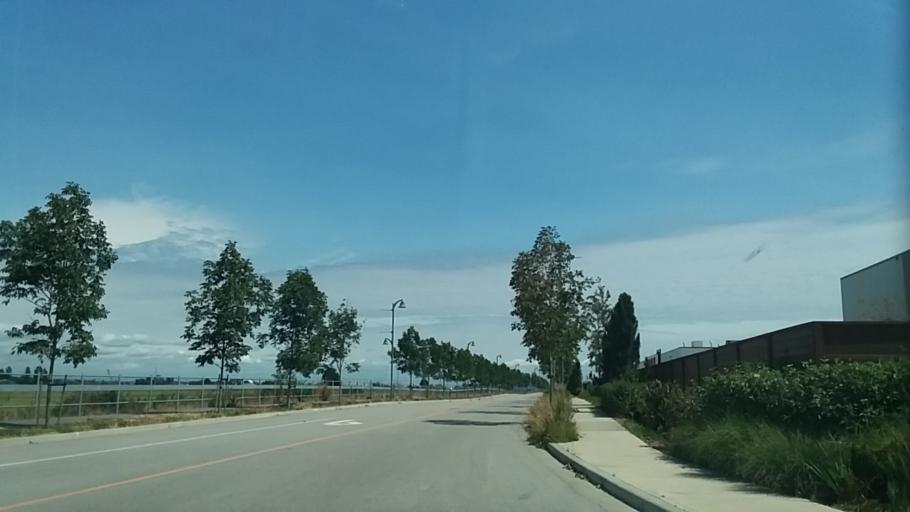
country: CA
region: British Columbia
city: Ladner
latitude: 49.0431
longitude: -123.0900
